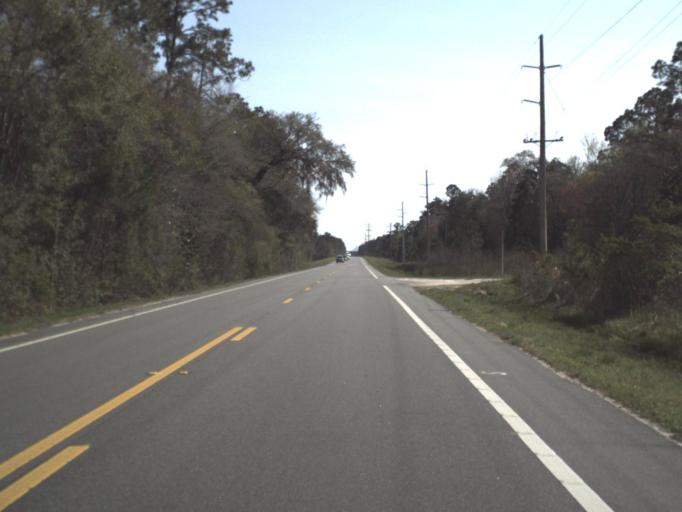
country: US
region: Florida
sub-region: Franklin County
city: Carrabelle
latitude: 29.9943
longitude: -84.5035
